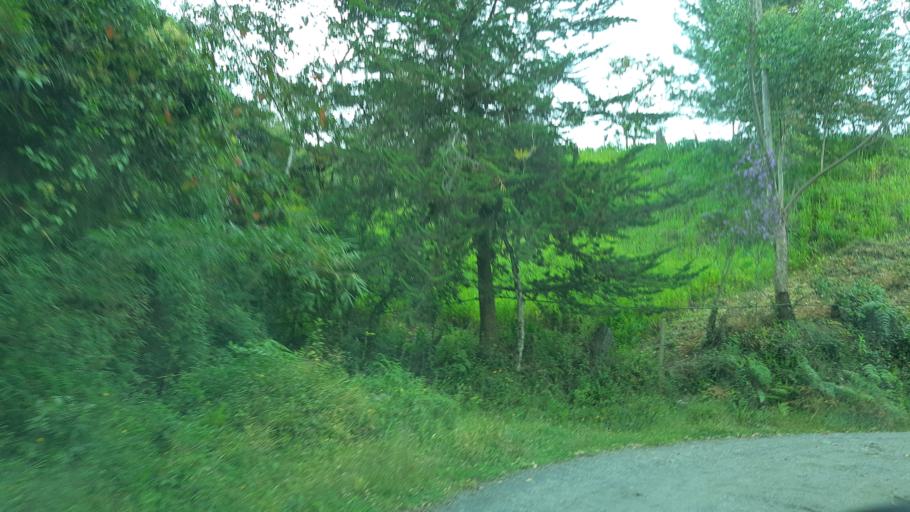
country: CO
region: Boyaca
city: Garagoa
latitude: 4.9936
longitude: -73.3277
